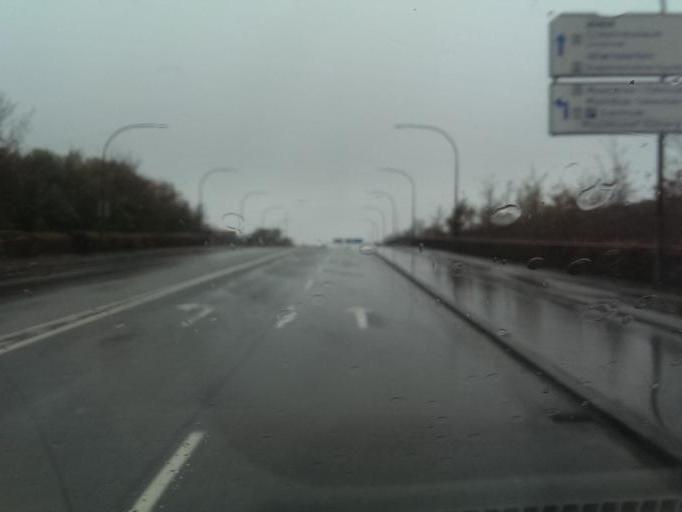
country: DK
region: South Denmark
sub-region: Esbjerg Kommune
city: Esbjerg
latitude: 55.4710
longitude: 8.4625
